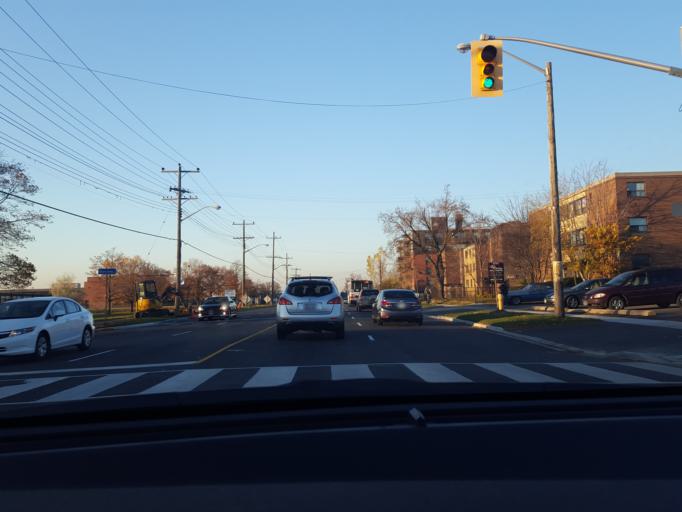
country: CA
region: Ontario
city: Scarborough
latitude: 43.7589
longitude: -79.2895
